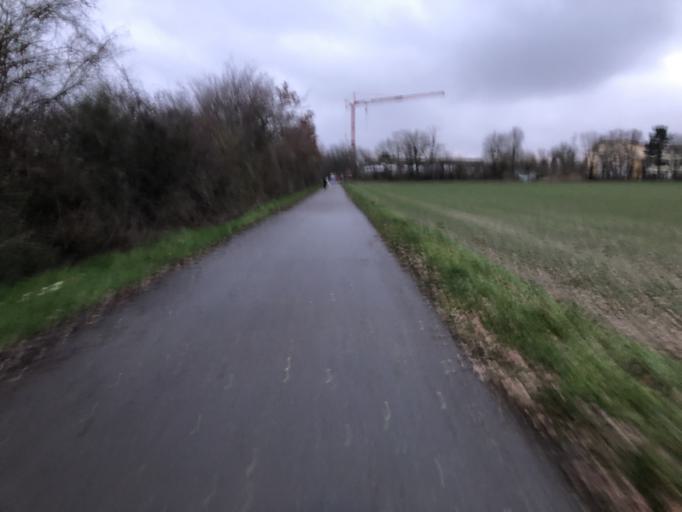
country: DE
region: Baden-Wuerttemberg
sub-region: Karlsruhe Region
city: Altlussheim
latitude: 49.3033
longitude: 8.5081
